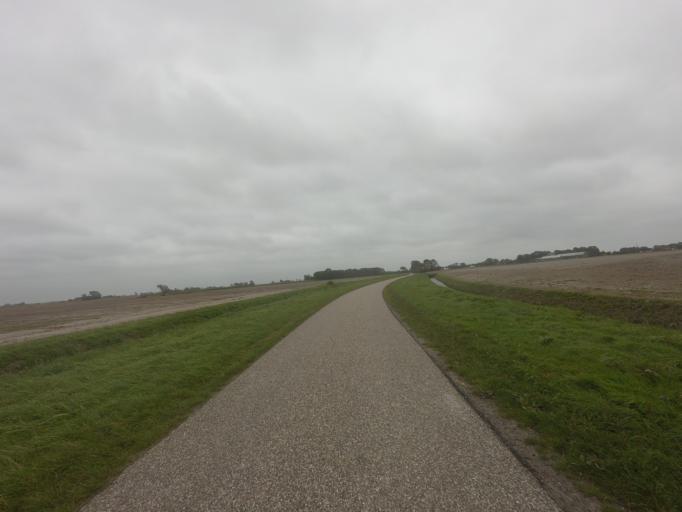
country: NL
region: Friesland
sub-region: Gemeente Ferwerderadiel
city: Ferwert
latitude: 53.3426
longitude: 5.8576
